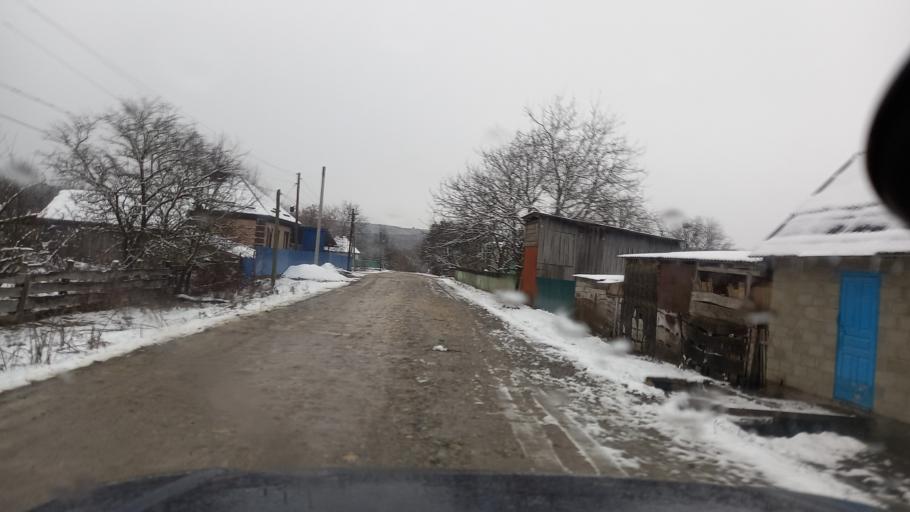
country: RU
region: Adygeya
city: Abadzekhskaya
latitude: 44.3510
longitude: 40.4142
